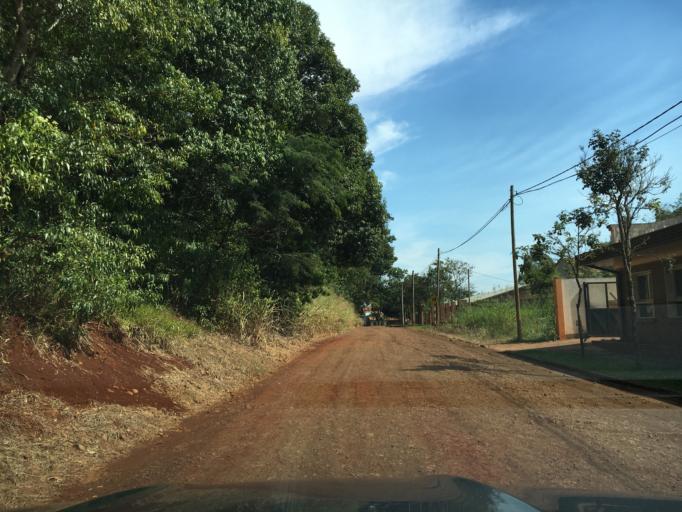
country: AR
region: Misiones
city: Puerto Rico
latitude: -26.8048
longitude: -54.9967
